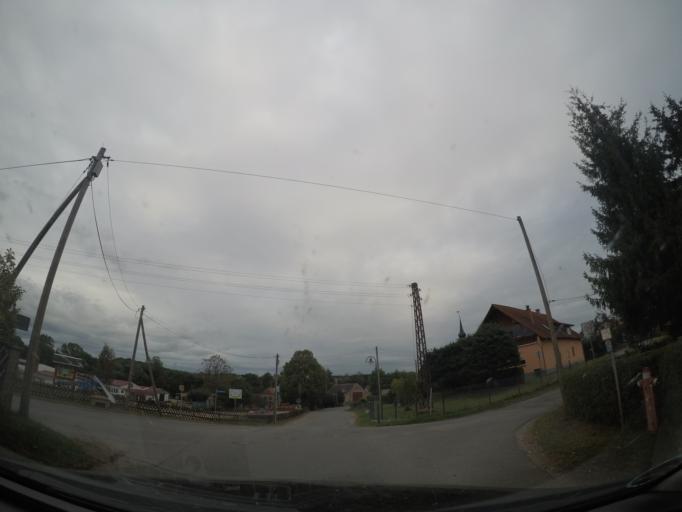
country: DE
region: Thuringia
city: Nobdenitz
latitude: 50.8841
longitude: 12.2889
